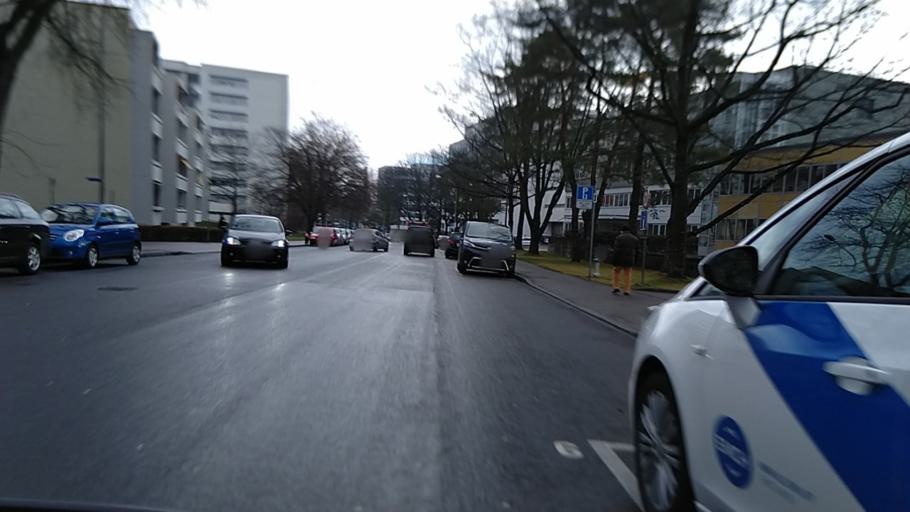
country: CH
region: Bern
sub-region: Bern-Mittelland District
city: Koniz
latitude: 46.9468
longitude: 7.3857
